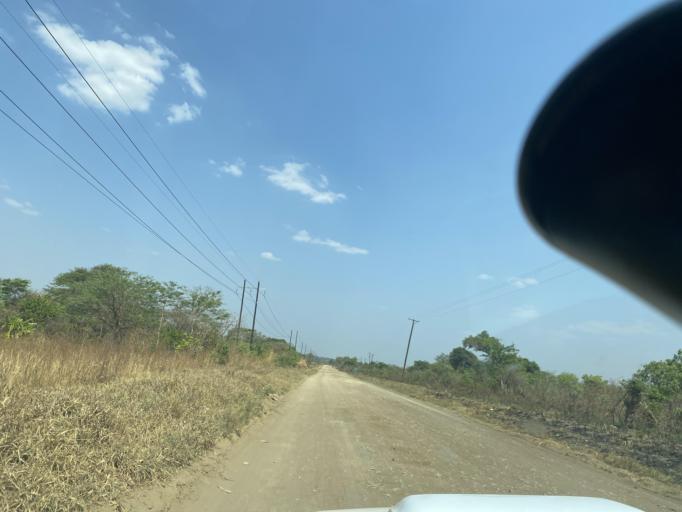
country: ZM
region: Lusaka
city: Lusaka
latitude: -15.3113
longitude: 28.0498
